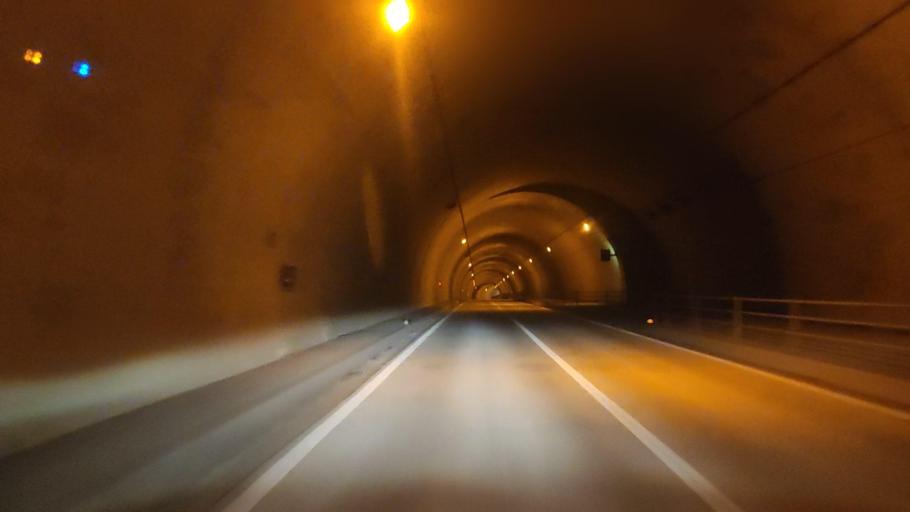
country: JP
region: Kumamoto
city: Hitoyoshi
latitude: 32.3901
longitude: 130.8312
